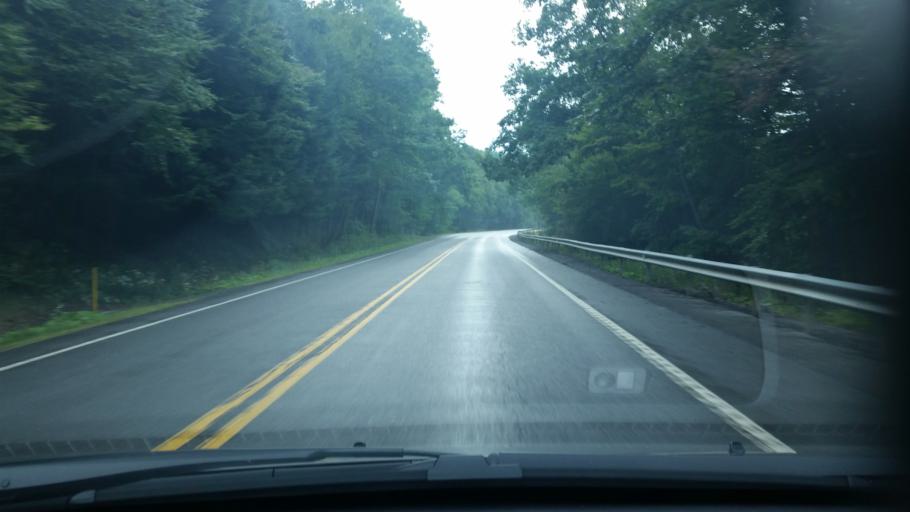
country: US
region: Pennsylvania
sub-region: Clearfield County
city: Shiloh
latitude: 41.0856
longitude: -78.2536
